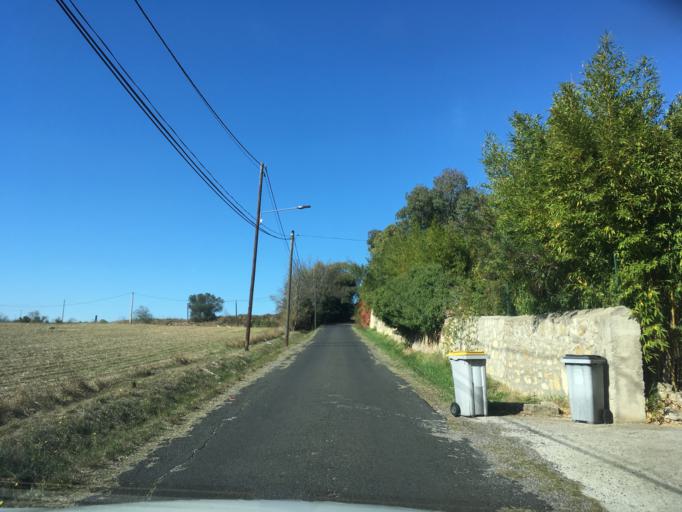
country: FR
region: Languedoc-Roussillon
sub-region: Departement de l'Herault
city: Saint-Jean-de-Vedas
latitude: 43.5977
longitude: 3.8283
